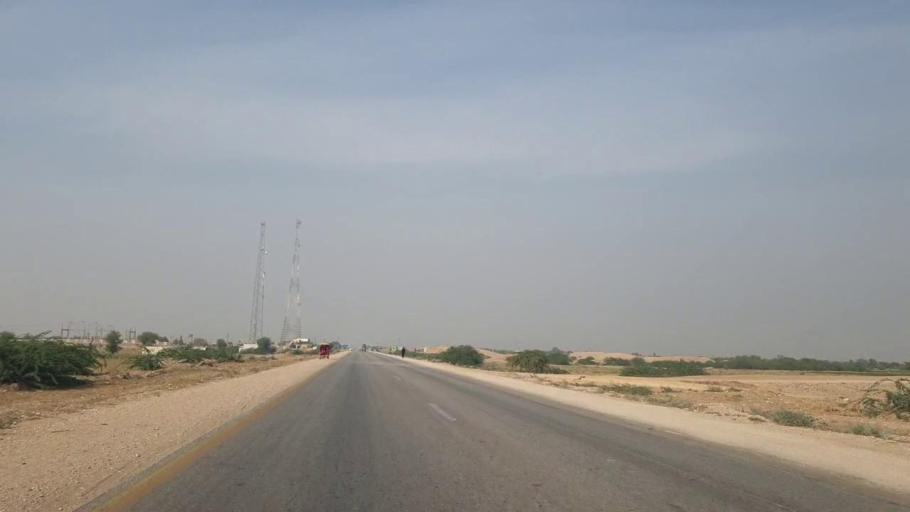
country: PK
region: Sindh
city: Sann
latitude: 26.0511
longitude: 68.1081
